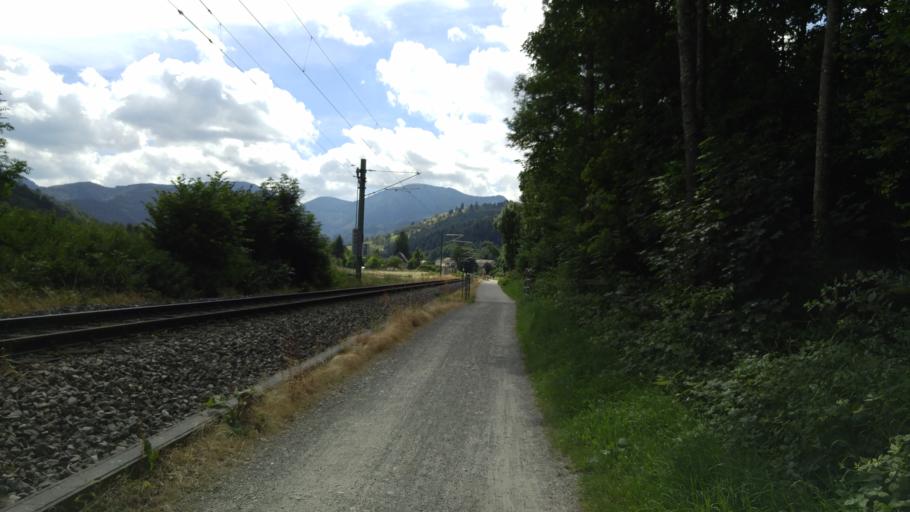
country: DE
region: Baden-Wuerttemberg
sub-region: Freiburg Region
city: Muenstertal/Schwarzwald
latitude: 47.8625
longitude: 7.7572
